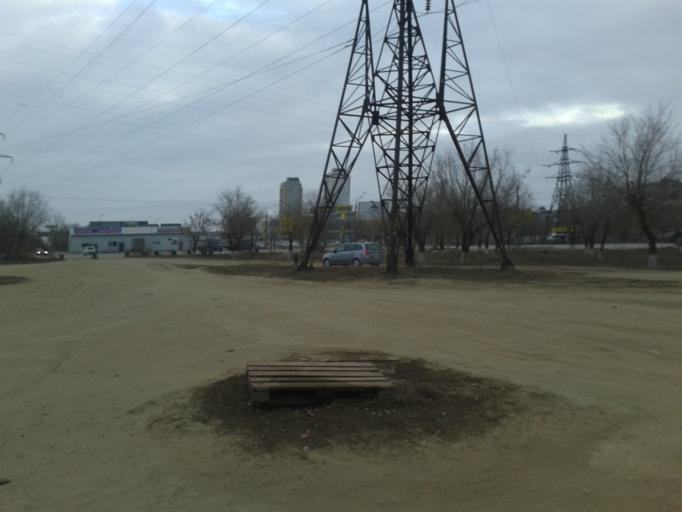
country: RU
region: Volgograd
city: Gorodishche
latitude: 48.7657
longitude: 44.4734
